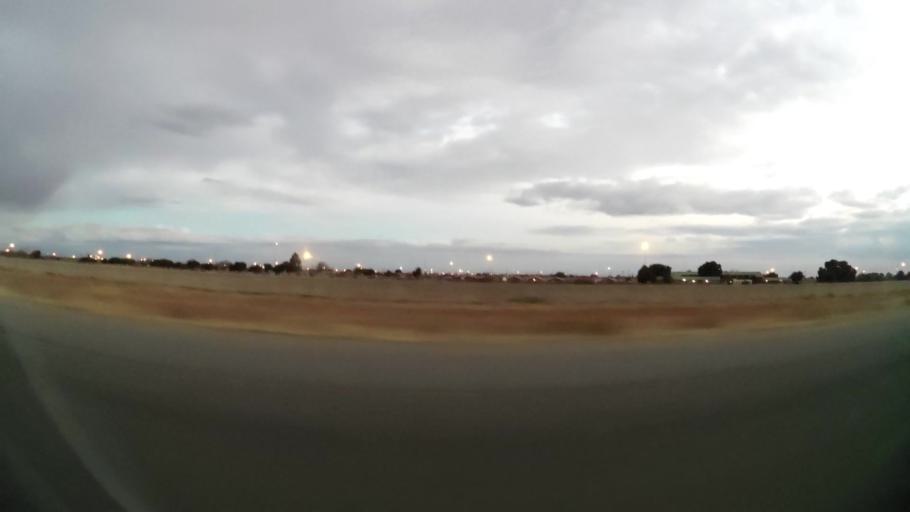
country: ZA
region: Orange Free State
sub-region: Lejweleputswa District Municipality
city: Welkom
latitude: -27.9519
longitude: 26.7913
